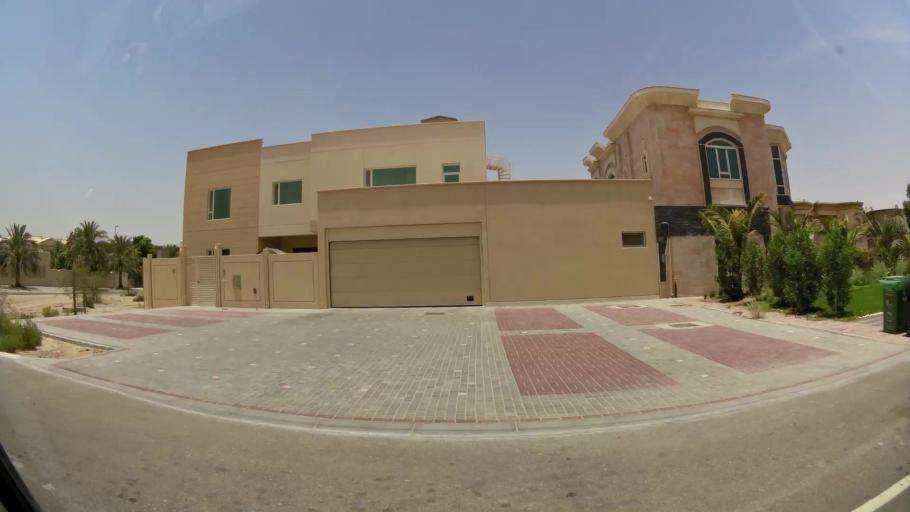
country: AE
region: Ash Shariqah
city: Sharjah
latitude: 25.2392
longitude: 55.4573
